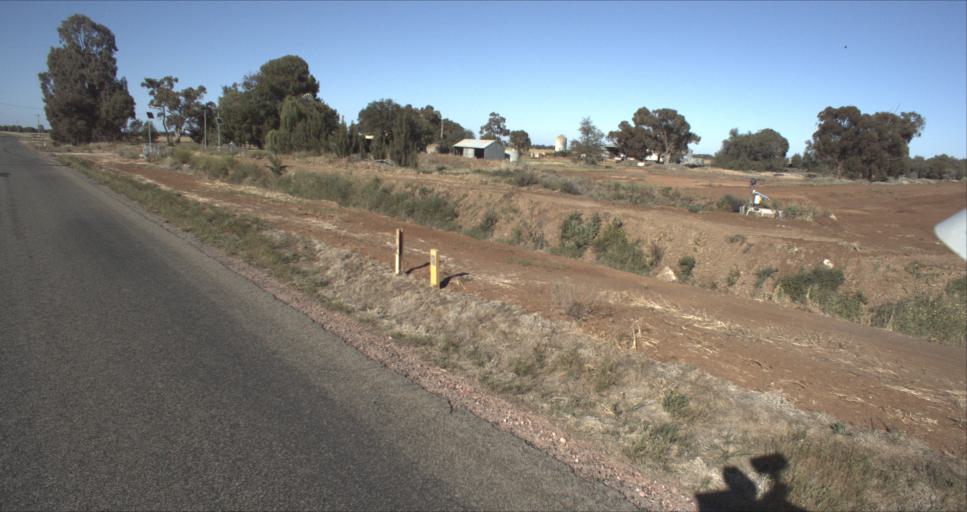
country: AU
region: New South Wales
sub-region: Leeton
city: Leeton
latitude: -34.5540
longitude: 146.2668
